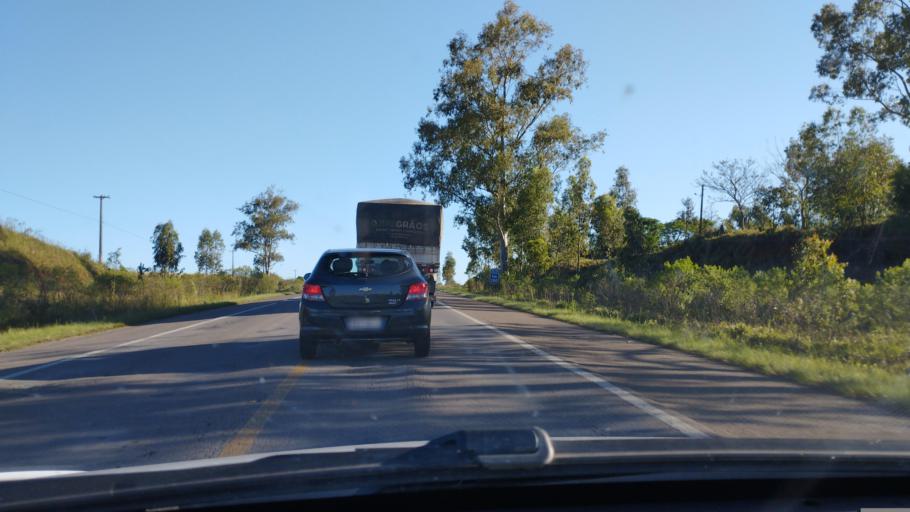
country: BR
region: Rio Grande do Sul
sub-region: Julio De Castilhos
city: Julio de Castilhos
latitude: -29.3765
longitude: -53.6707
